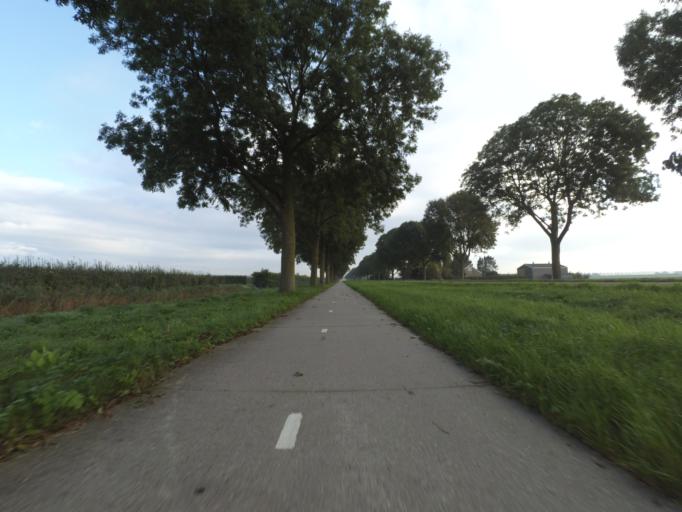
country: NL
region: Flevoland
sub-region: Gemeente Dronten
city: Dronten
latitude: 52.5045
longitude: 5.6819
